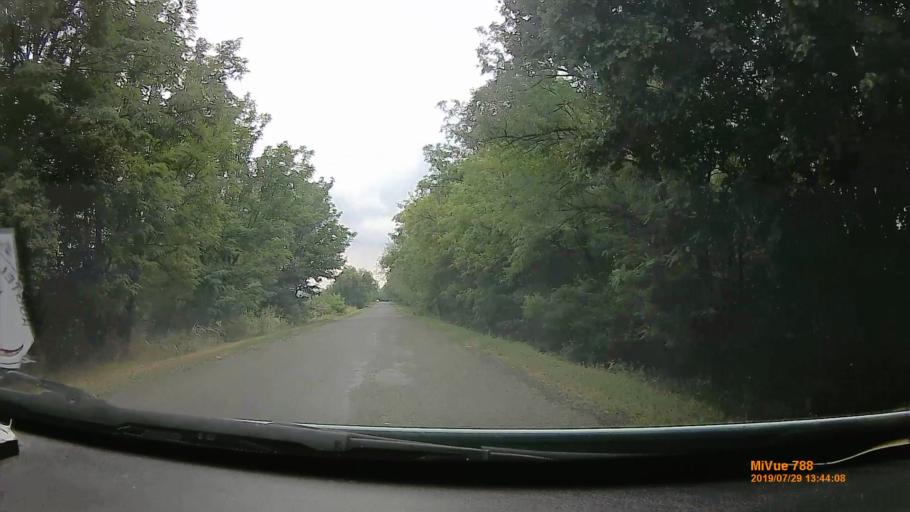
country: HU
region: Somogy
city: Balatonfoldvar
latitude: 46.7993
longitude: 17.9354
